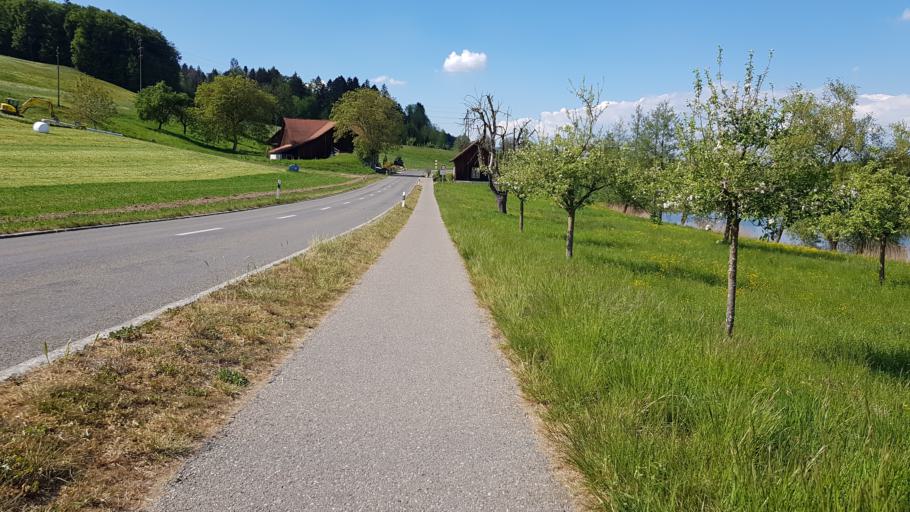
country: CH
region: Lucerne
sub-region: Hochdorf District
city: Hitzkirch
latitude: 47.2068
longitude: 8.2438
